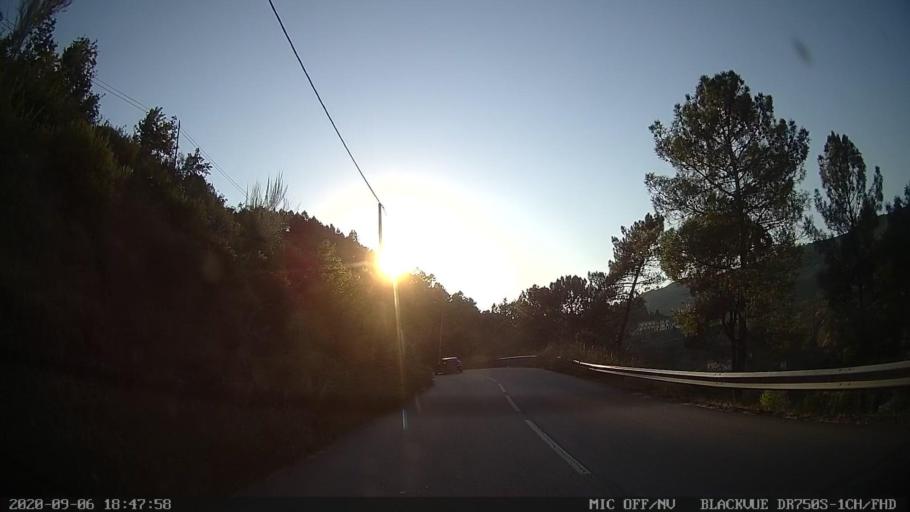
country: PT
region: Porto
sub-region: Amarante
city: Amarante
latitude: 41.2653
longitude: -8.0066
